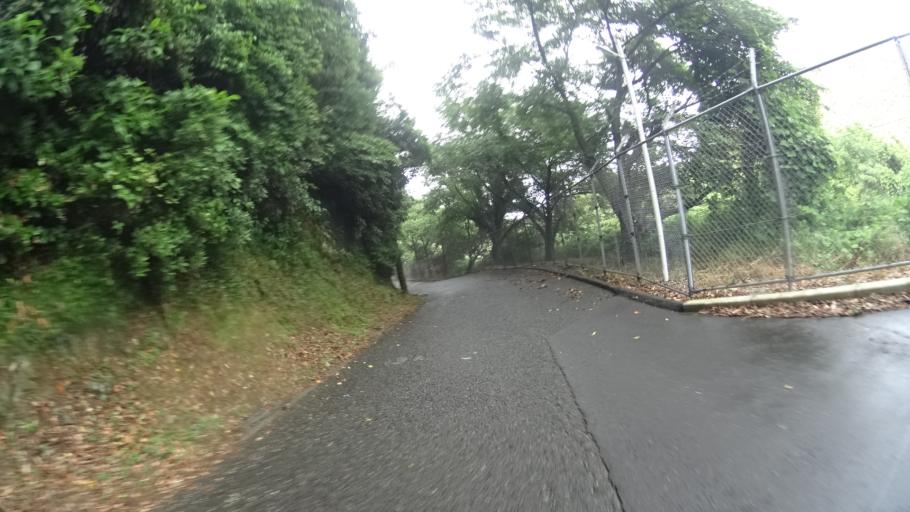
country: JP
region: Yamaguchi
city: Shimonoseki
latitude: 34.1091
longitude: 130.8663
